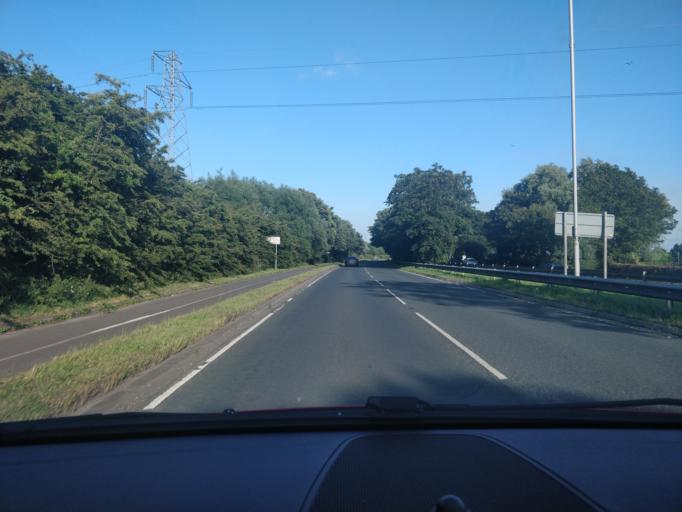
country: GB
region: England
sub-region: Lancashire
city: Banks
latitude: 53.6688
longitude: -2.9045
